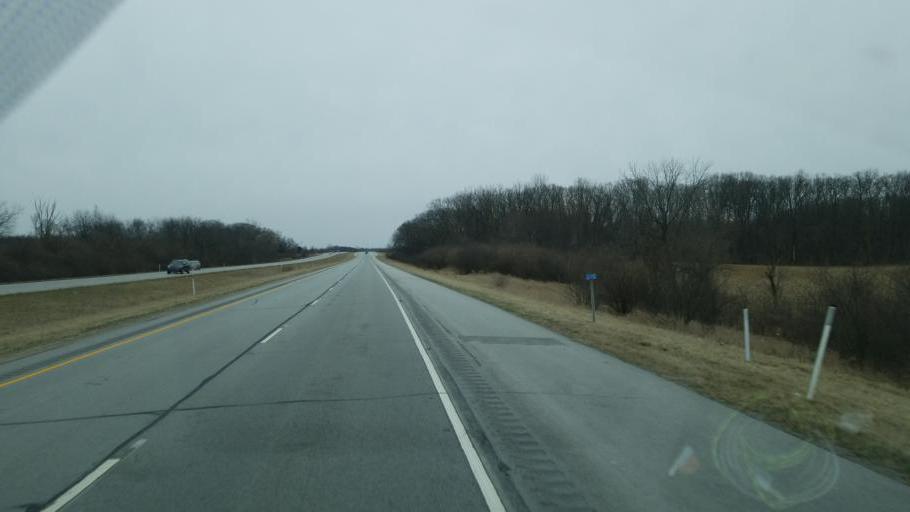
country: US
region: Indiana
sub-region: Marshall County
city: Argos
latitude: 41.2715
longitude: -86.2701
